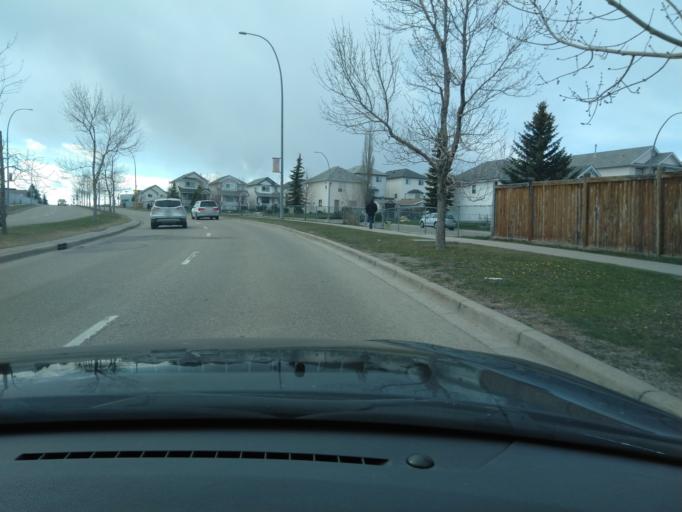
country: CA
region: Alberta
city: Calgary
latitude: 51.1340
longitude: -114.2056
